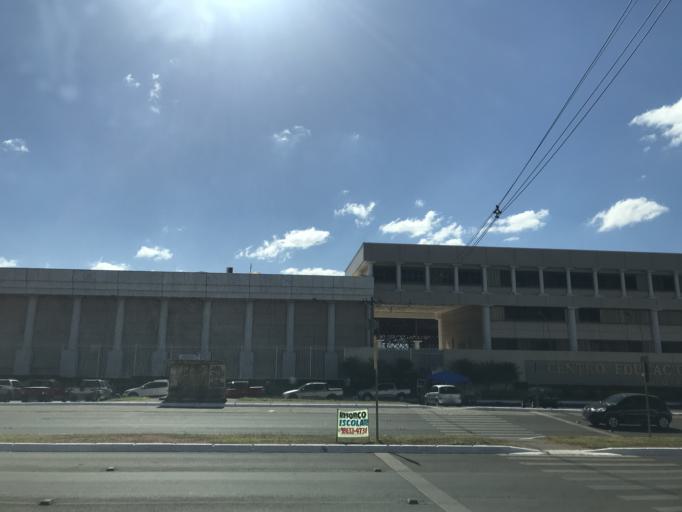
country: BR
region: Federal District
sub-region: Brasilia
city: Brasilia
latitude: -15.8481
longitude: -48.0407
